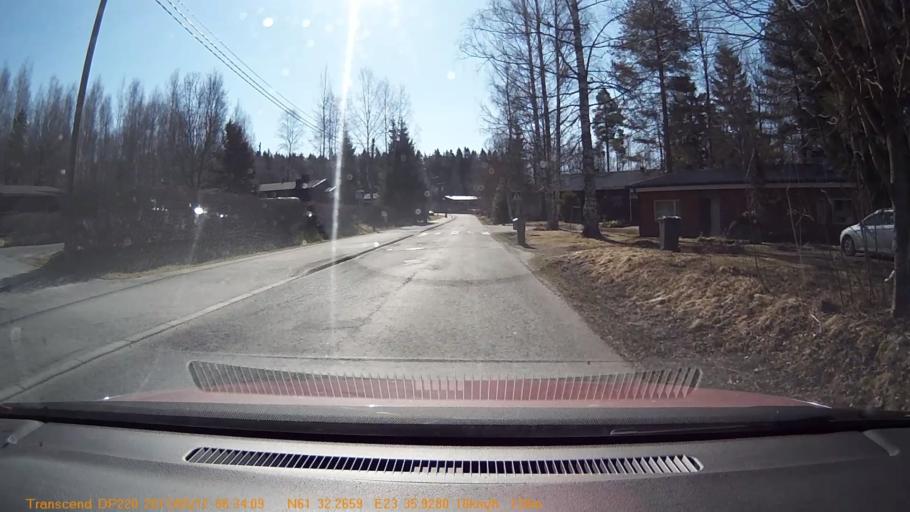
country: FI
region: Pirkanmaa
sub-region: Tampere
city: Yloejaervi
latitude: 61.5377
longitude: 23.5989
